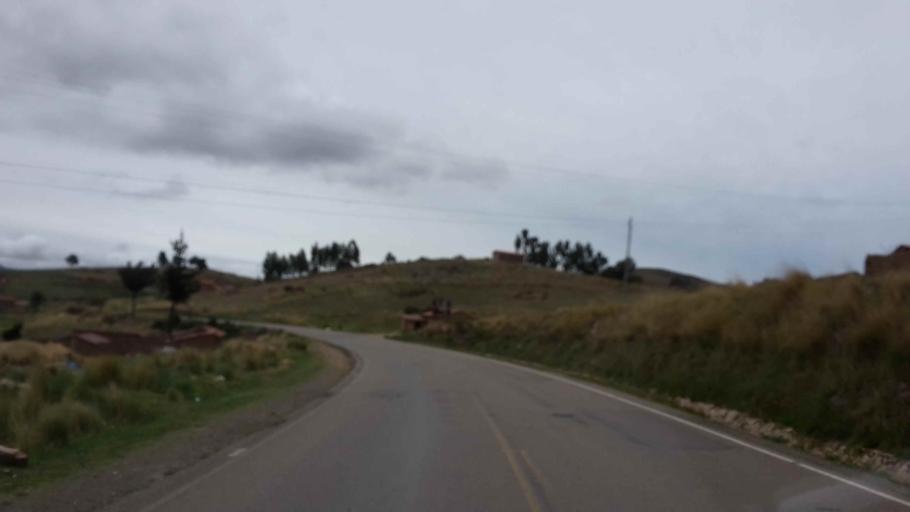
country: BO
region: Cochabamba
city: Arani
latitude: -17.4683
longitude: -65.6543
